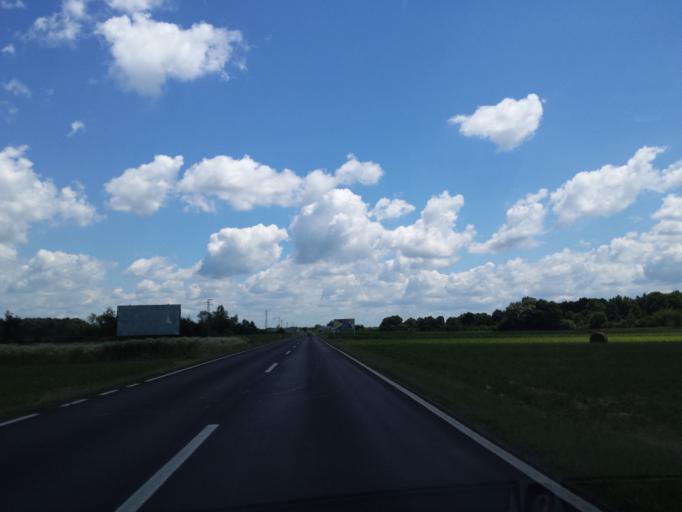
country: HR
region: Sisacko-Moslavacka
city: Petrinja
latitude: 45.5136
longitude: 16.2619
